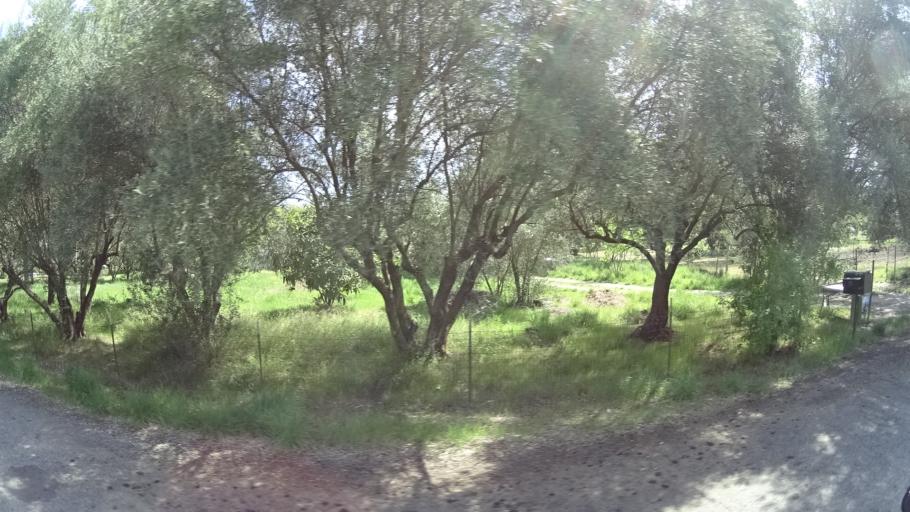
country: US
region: California
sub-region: Glenn County
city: Hamilton City
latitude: 39.8037
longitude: -122.0570
